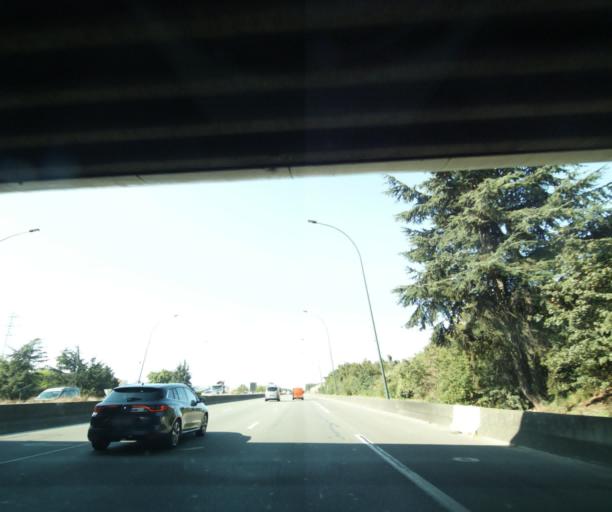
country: FR
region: Midi-Pyrenees
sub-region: Departement de la Haute-Garonne
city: Portet-sur-Garonne
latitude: 43.5546
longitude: 1.4099
